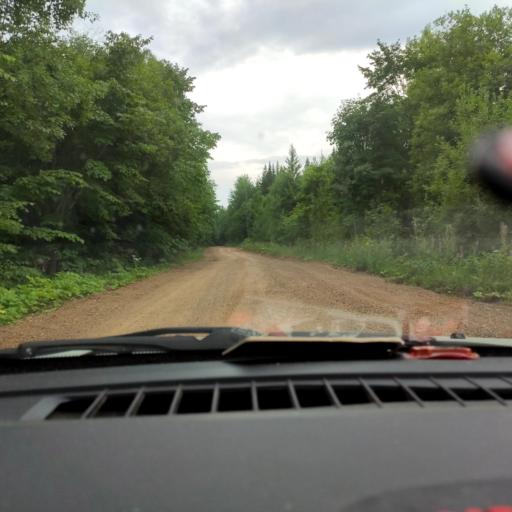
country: RU
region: Perm
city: Kultayevo
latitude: 57.8107
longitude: 56.0044
